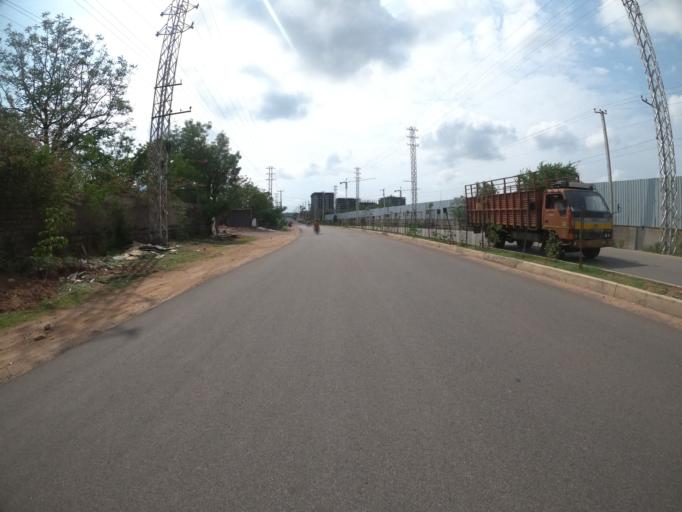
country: IN
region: Telangana
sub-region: Medak
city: Serilingampalle
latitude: 17.3898
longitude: 78.3263
